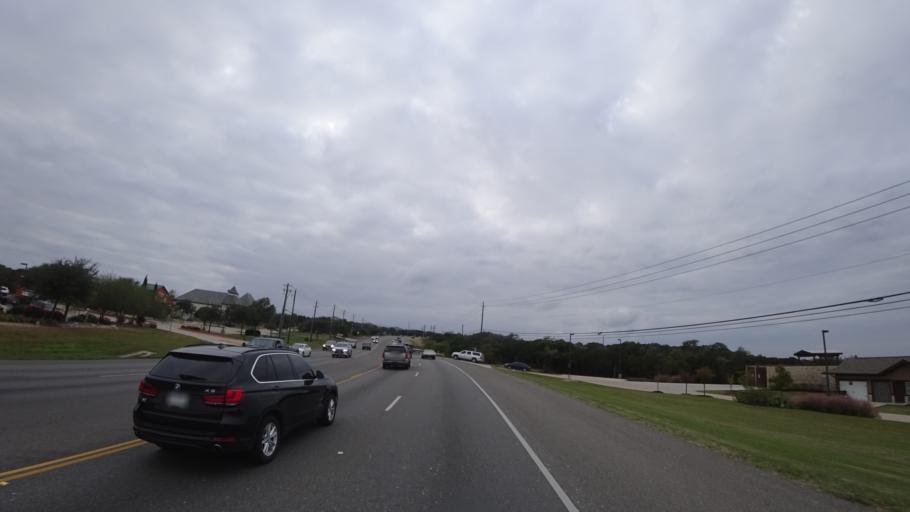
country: US
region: Texas
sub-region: Travis County
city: Bee Cave
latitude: 30.3253
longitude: -97.9588
